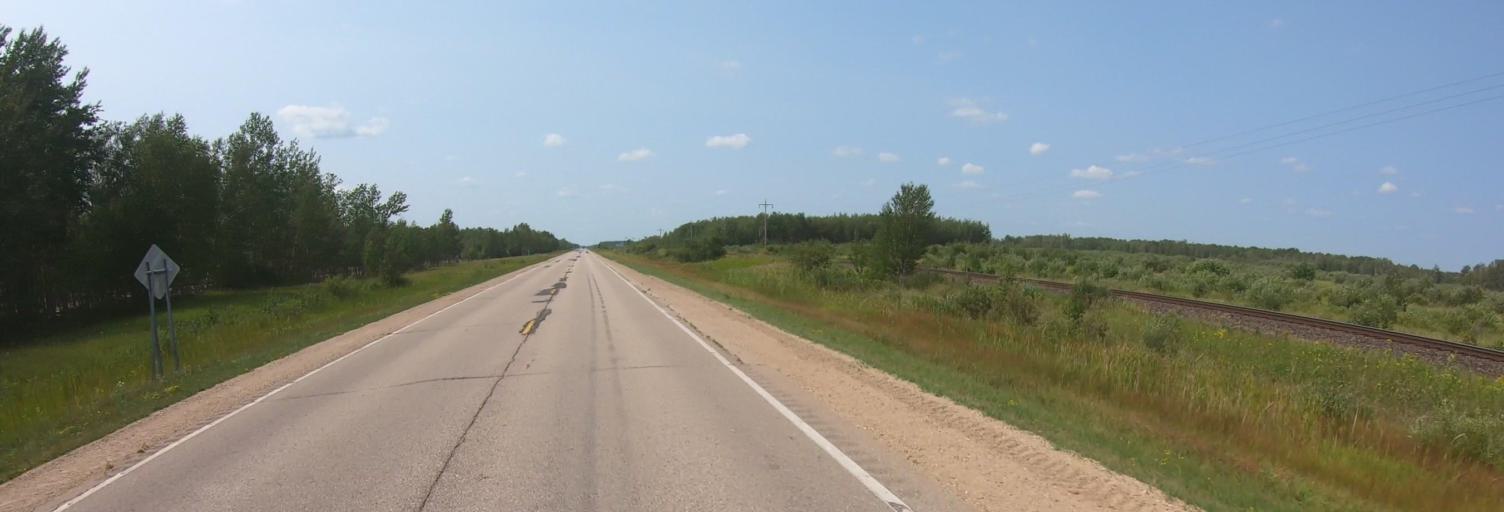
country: US
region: Minnesota
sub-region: Lake of the Woods County
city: Baudette
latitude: 48.7488
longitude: -94.8745
